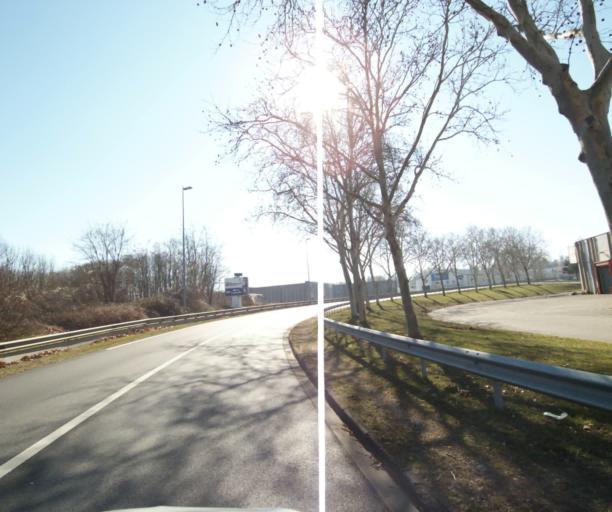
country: FR
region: Lorraine
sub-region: Departement de Meurthe-et-Moselle
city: Jarville-la-Malgrange
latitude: 48.6694
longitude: 6.2143
